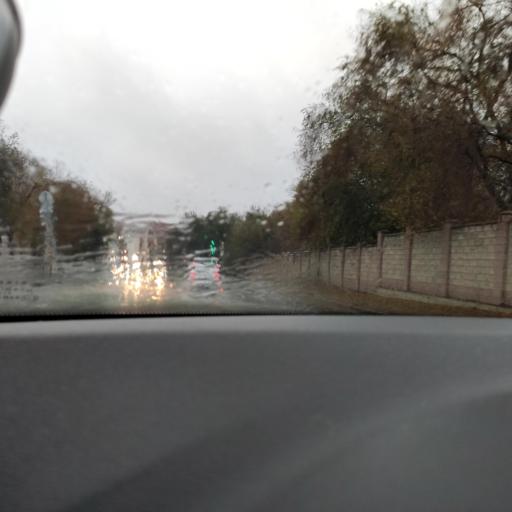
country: RU
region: Samara
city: Petra-Dubrava
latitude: 53.2419
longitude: 50.2731
